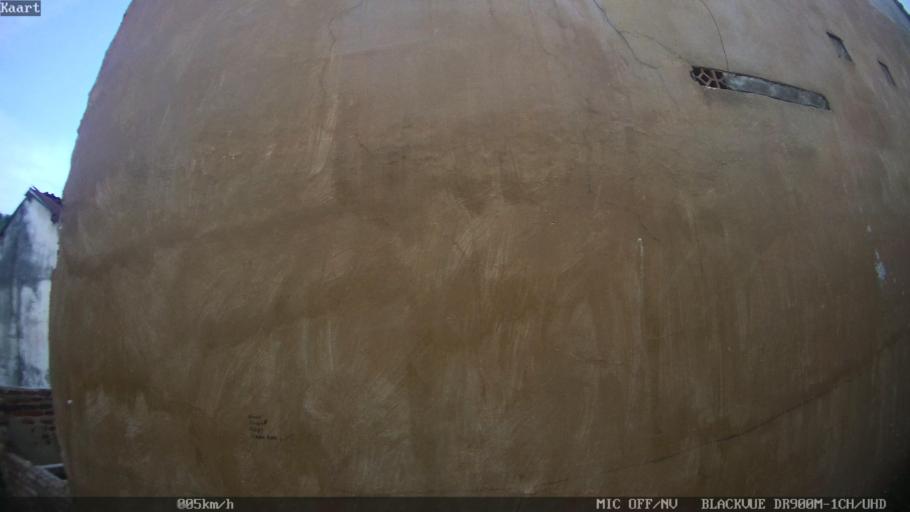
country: ID
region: Lampung
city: Kedaton
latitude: -5.4026
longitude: 105.2964
